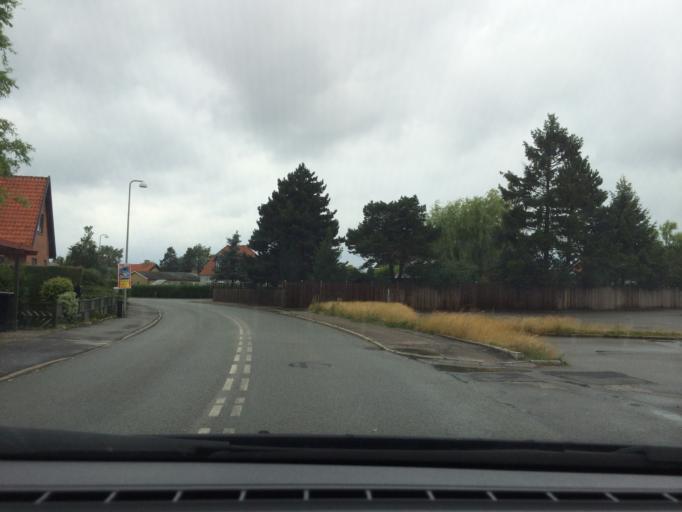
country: DK
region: Zealand
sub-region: Vordingborg Kommune
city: Stege
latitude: 54.9920
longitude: 12.2897
